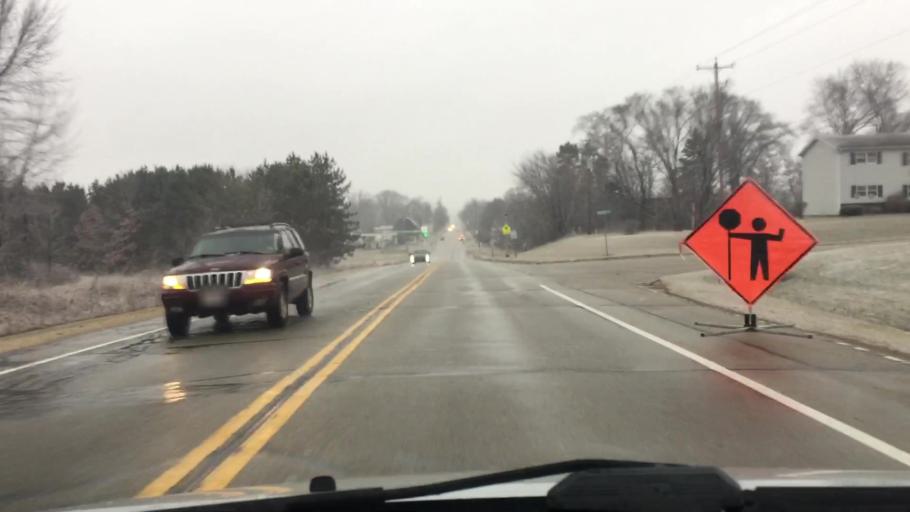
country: US
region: Wisconsin
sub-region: Dodge County
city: Hustisford
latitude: 43.3035
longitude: -88.5185
